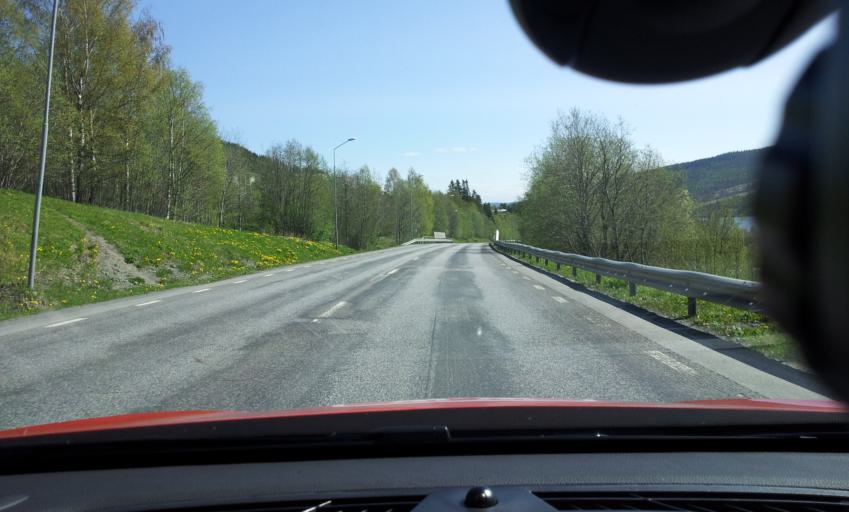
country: SE
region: Jaemtland
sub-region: Are Kommun
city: Are
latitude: 63.3977
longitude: 13.0877
